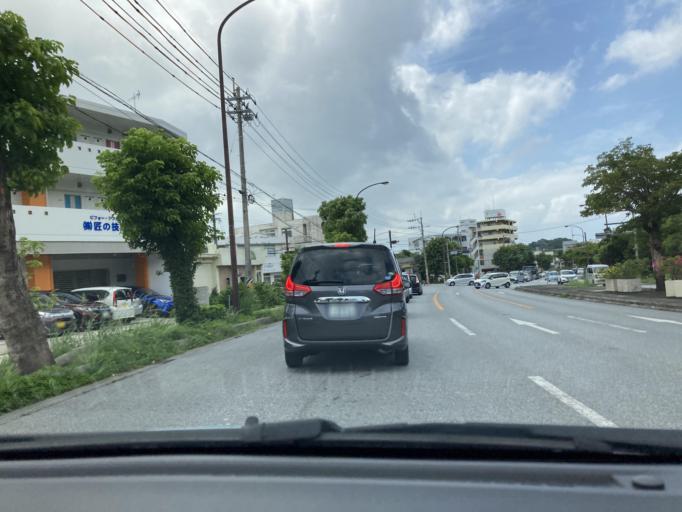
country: JP
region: Okinawa
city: Chatan
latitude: 26.2964
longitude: 127.7852
